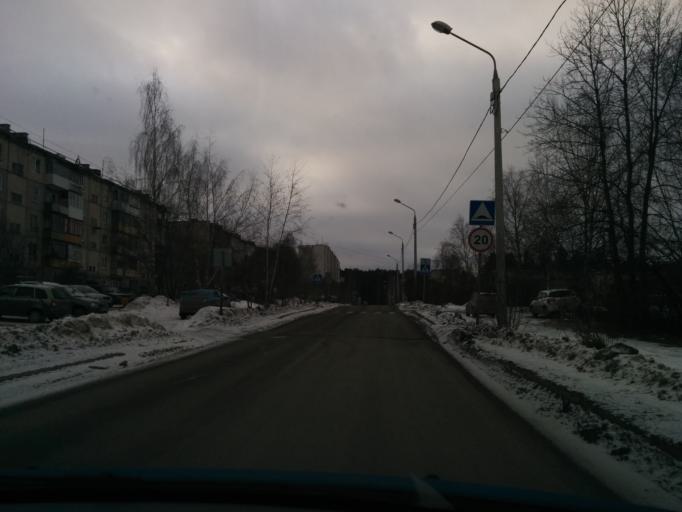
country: RU
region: Perm
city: Kondratovo
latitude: 58.0258
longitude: 56.0079
